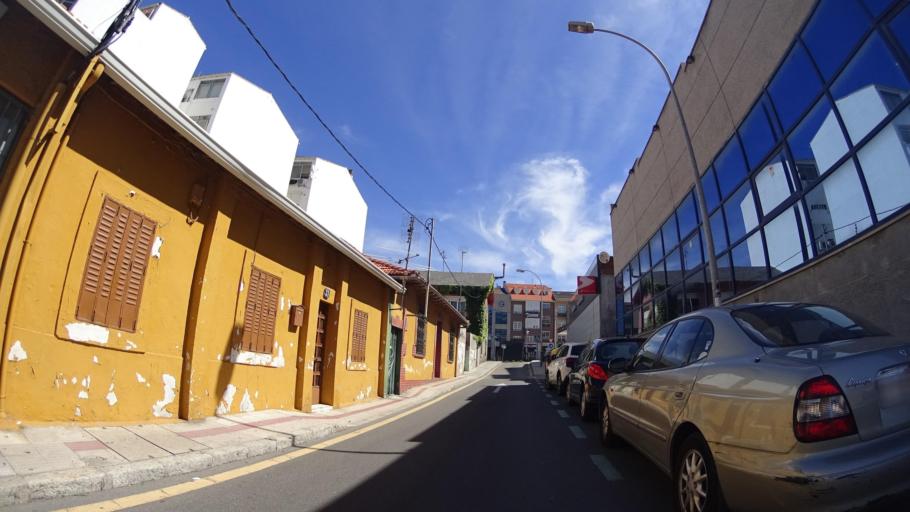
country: ES
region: Madrid
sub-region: Provincia de Madrid
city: Collado-Villalba
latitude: 40.6297
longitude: -4.0043
